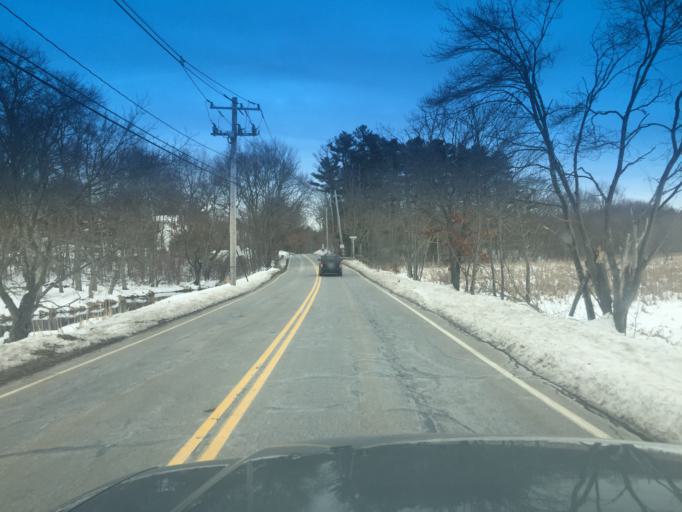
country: US
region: Massachusetts
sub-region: Norfolk County
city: Norfolk
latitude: 42.1183
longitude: -71.2970
